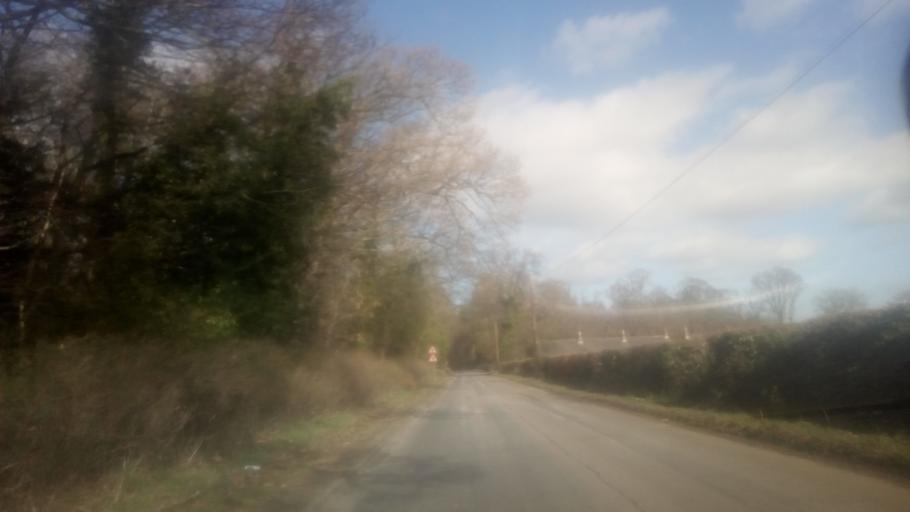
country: GB
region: Scotland
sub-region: Fife
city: Pathhead
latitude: 55.8809
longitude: -2.9601
